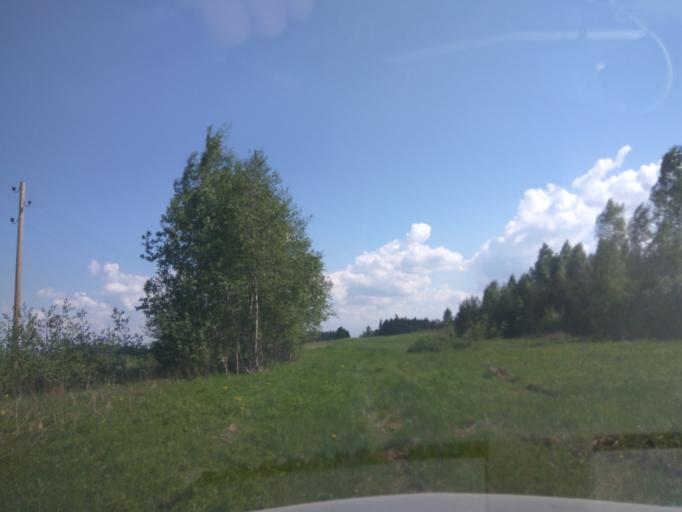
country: LV
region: Kuldigas Rajons
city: Kuldiga
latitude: 57.1787
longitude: 22.0071
